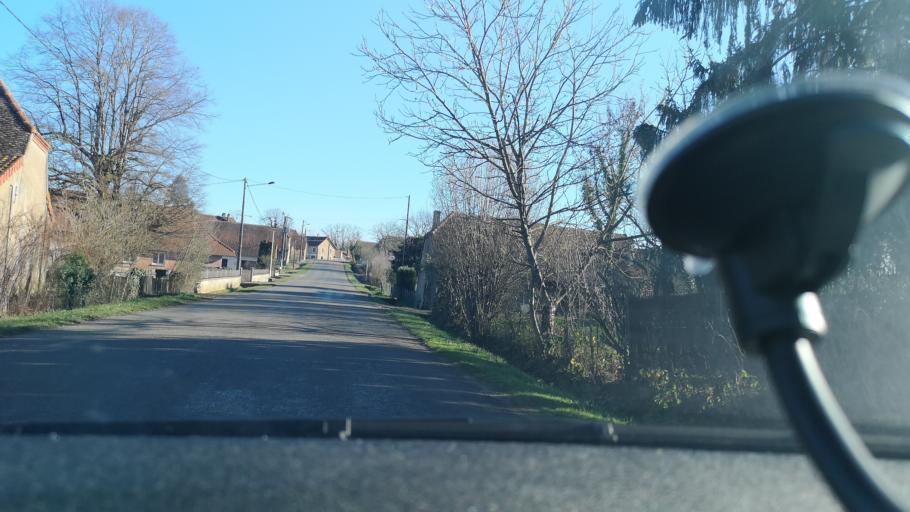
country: FR
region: Bourgogne
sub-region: Departement de Saone-et-Loire
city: Saint-Germain-du-Bois
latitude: 46.7451
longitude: 5.3125
